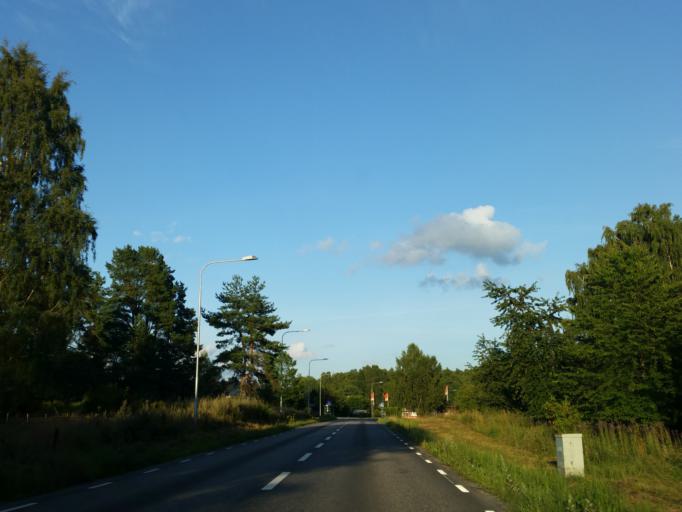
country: SE
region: Stockholm
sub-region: Nykvarns Kommun
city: Nykvarn
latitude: 59.2522
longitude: 17.5194
